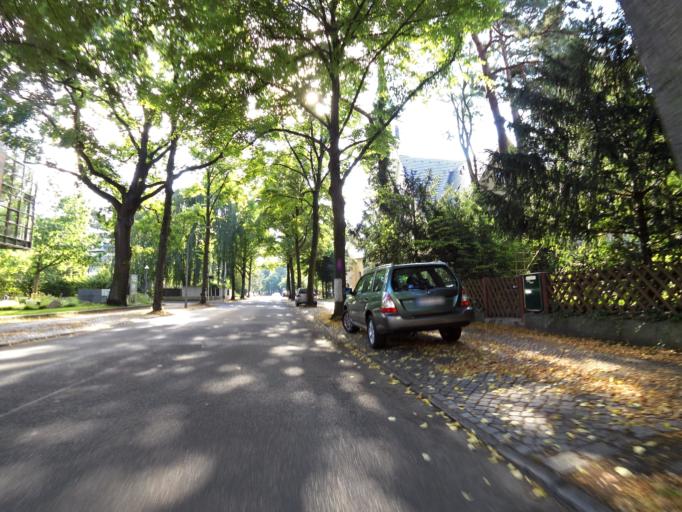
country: DE
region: Berlin
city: Nikolassee
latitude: 52.4381
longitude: 13.2187
